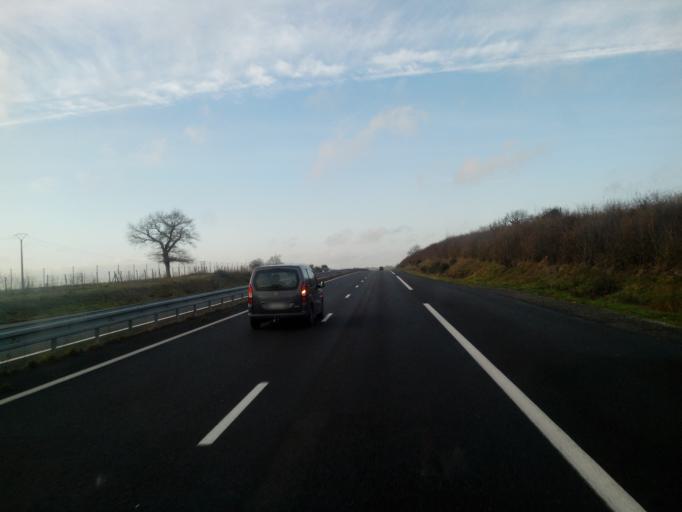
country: FR
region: Poitou-Charentes
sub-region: Departement des Deux-Sevres
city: Le Pin
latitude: 46.9033
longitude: -0.6688
